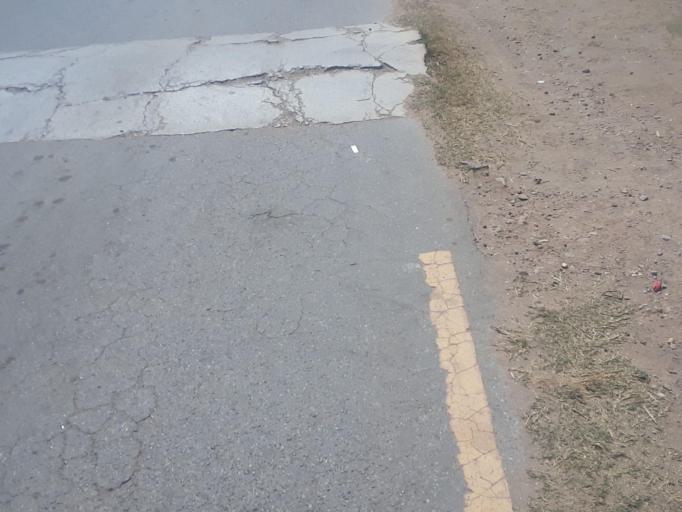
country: ZM
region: Lusaka
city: Lusaka
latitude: -15.3590
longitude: 28.2785
